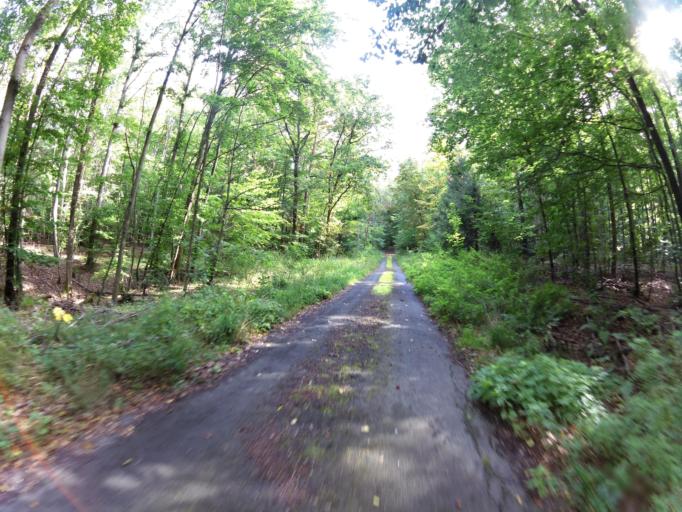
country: DE
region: Bavaria
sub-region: Regierungsbezirk Unterfranken
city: Waldbrunn
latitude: 49.7233
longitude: 9.7985
